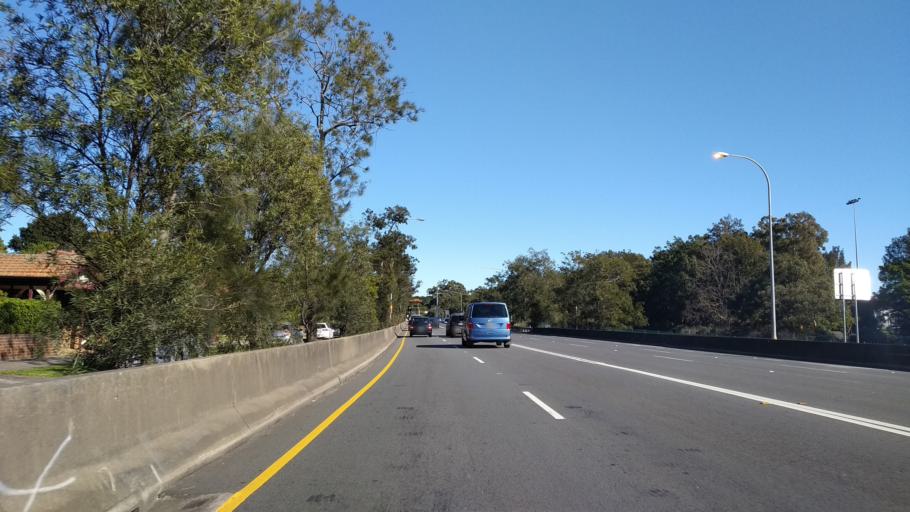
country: AU
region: New South Wales
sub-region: Canada Bay
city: Wareemba
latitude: -33.8711
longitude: 151.1413
